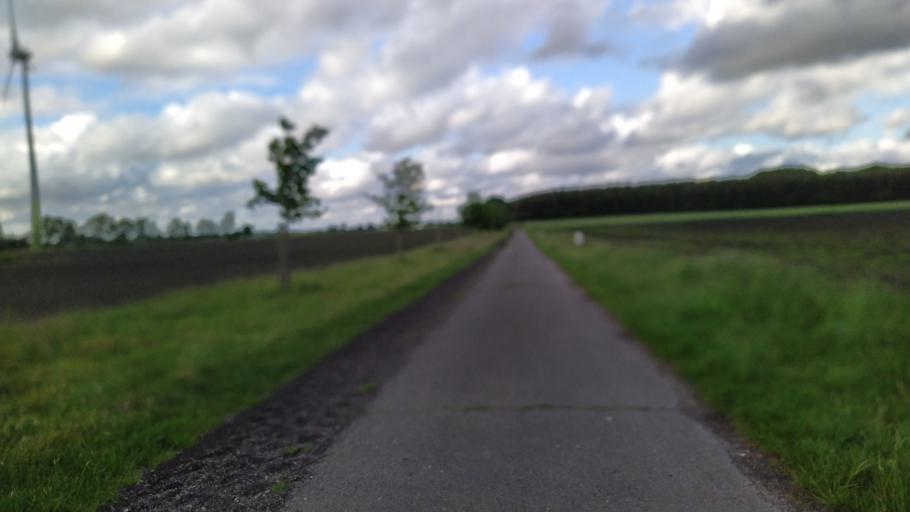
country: DE
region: Lower Saxony
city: Farven
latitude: 53.4537
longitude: 9.2996
